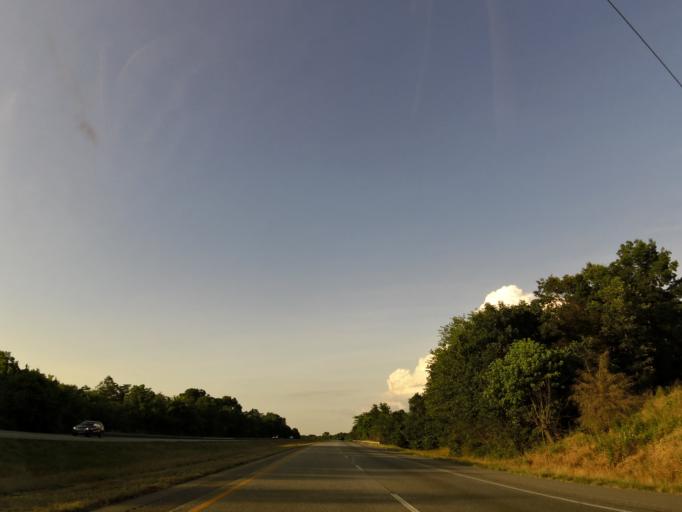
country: US
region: Georgia
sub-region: Dade County
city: Trenton
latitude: 34.8186
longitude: -85.5427
